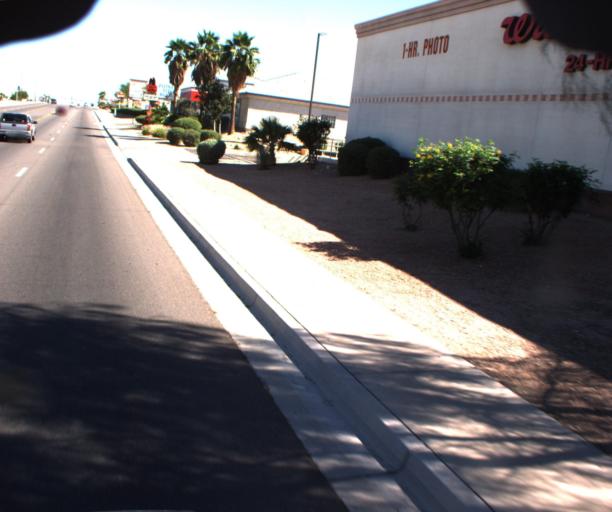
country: US
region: Arizona
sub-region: Mohave County
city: Bullhead City
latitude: 35.1014
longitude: -114.5979
